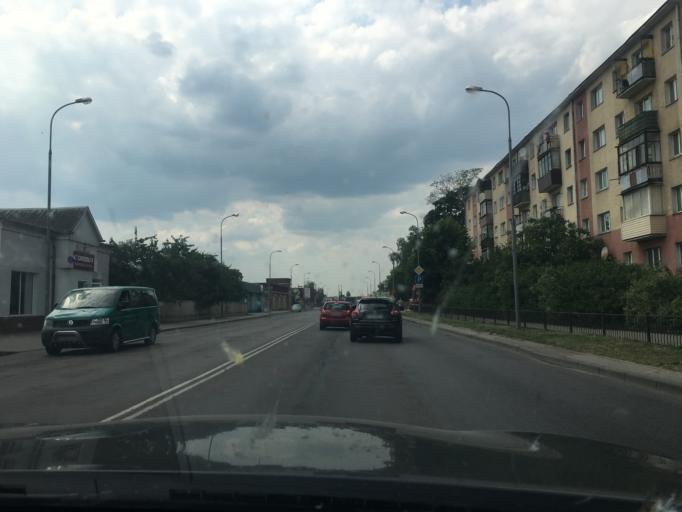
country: BY
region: Brest
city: Brest
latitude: 52.1028
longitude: 23.6736
